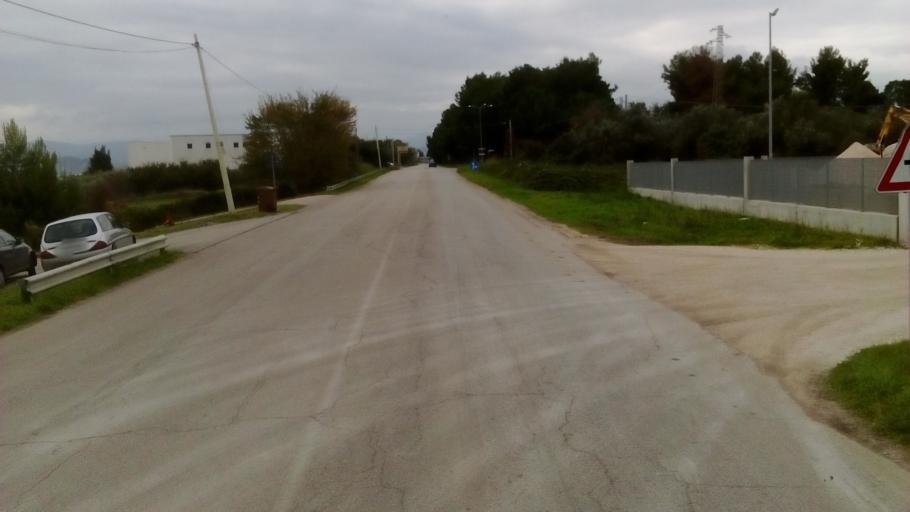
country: IT
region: Abruzzo
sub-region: Provincia di Chieti
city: San Salvo
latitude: 42.0427
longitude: 14.7529
